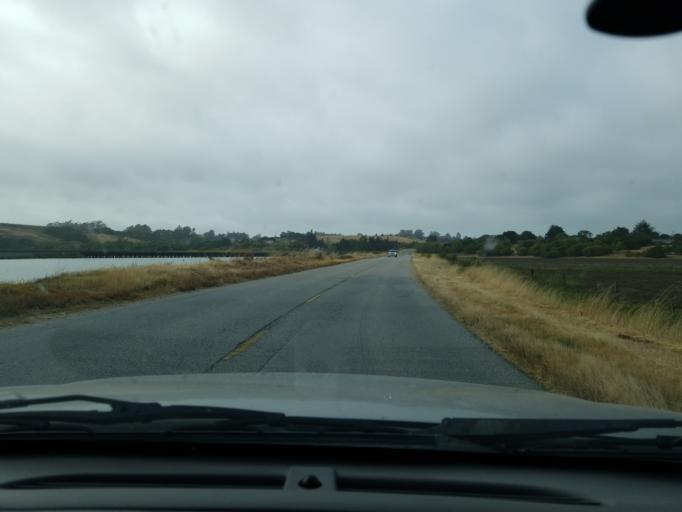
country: US
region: California
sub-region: Monterey County
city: Las Lomas
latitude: 36.8547
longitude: -121.7550
